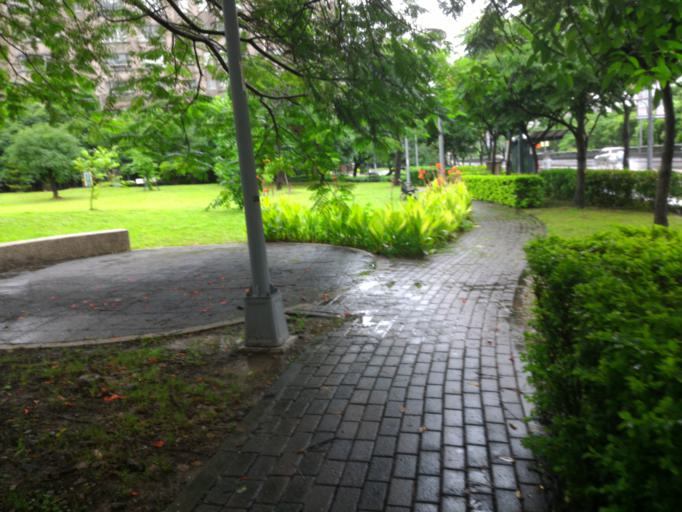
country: TW
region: Taiwan
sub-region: Taoyuan
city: Taoyuan
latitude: 24.9415
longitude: 121.3696
